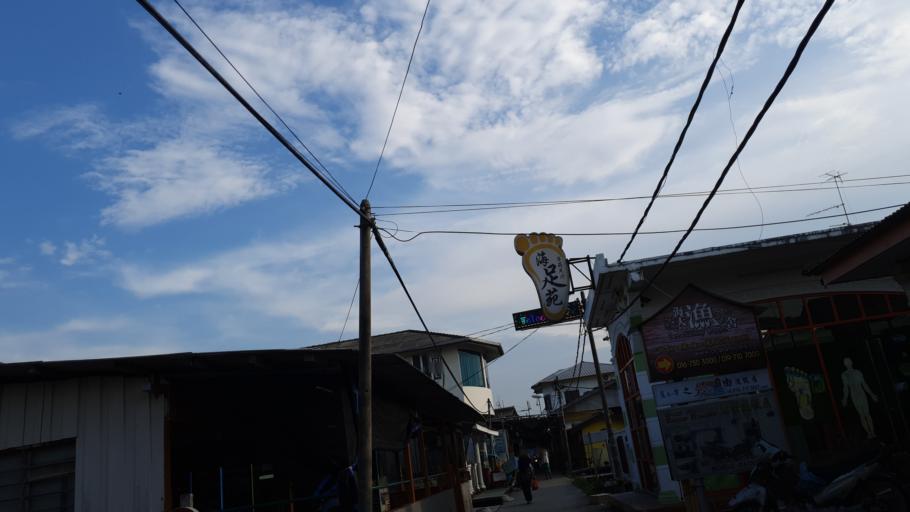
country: MY
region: Johor
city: Pontian Kechil
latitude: 1.3267
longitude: 103.4430
